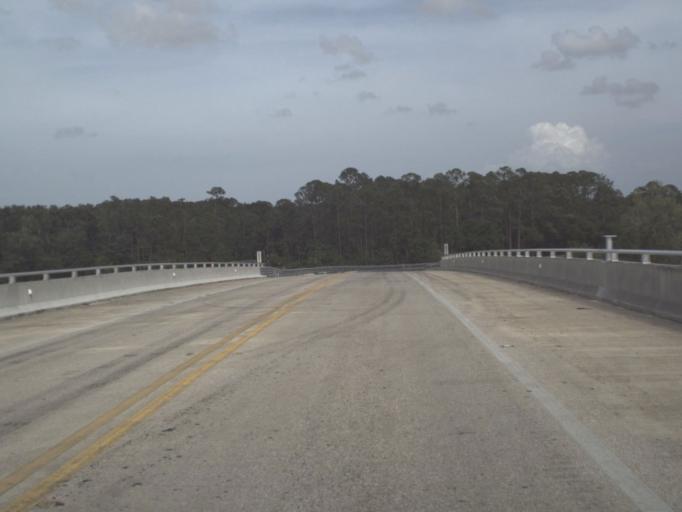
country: US
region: Florida
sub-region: Flagler County
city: Bunnell
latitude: 29.4721
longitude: -81.2670
